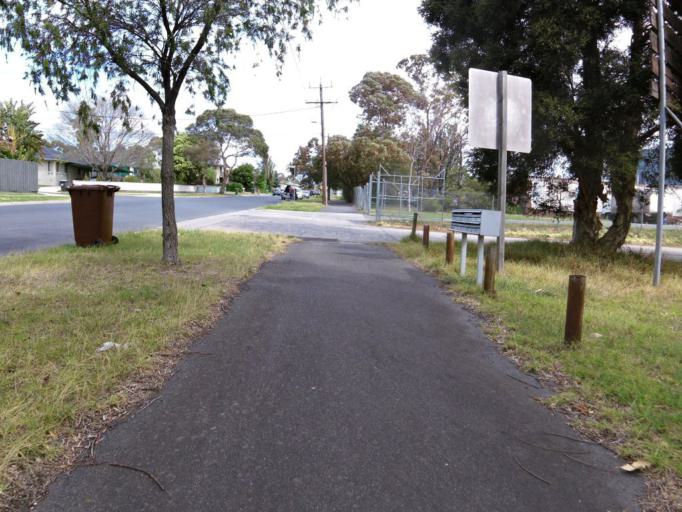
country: AU
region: Victoria
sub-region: Maroondah
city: Heathmont
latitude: -37.8416
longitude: 145.2490
